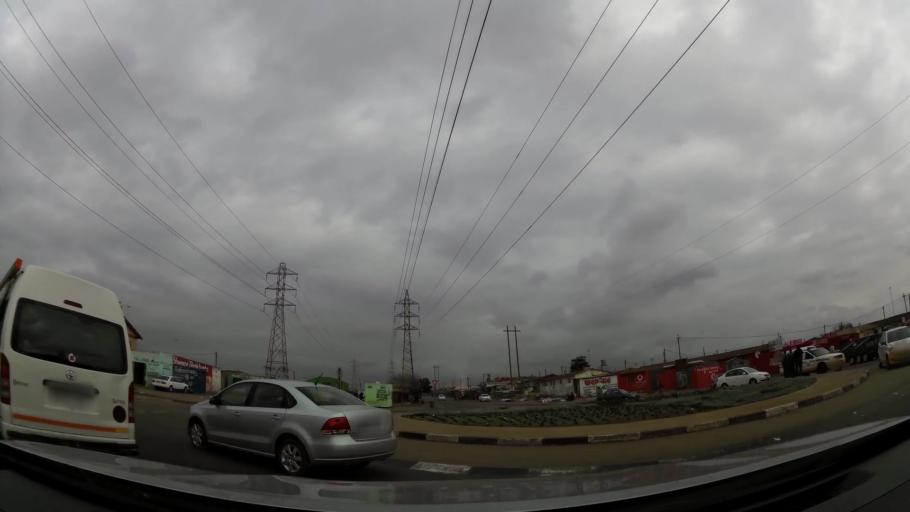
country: ZA
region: Eastern Cape
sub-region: Nelson Mandela Bay Metropolitan Municipality
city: Port Elizabeth
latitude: -33.8847
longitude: 25.5831
